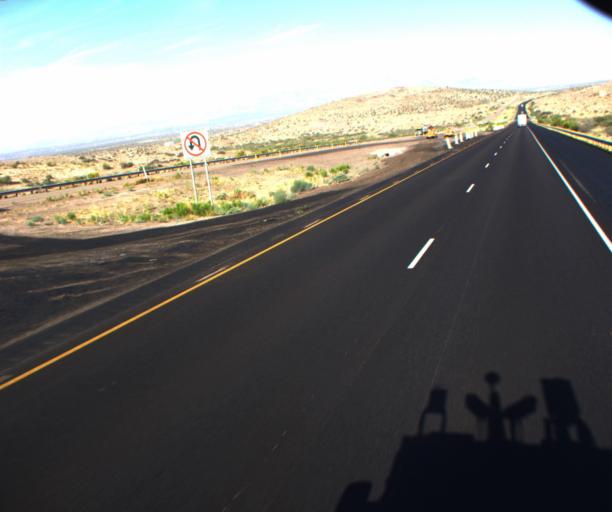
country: US
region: Arizona
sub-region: Mohave County
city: New Kingman-Butler
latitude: 35.1604
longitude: -113.6313
